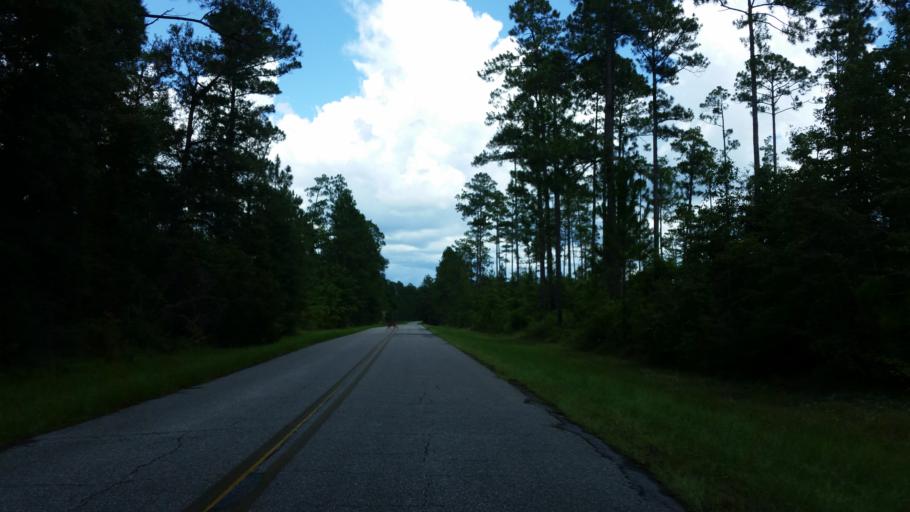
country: US
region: Florida
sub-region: Santa Rosa County
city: Point Baker
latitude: 30.7434
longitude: -86.8317
